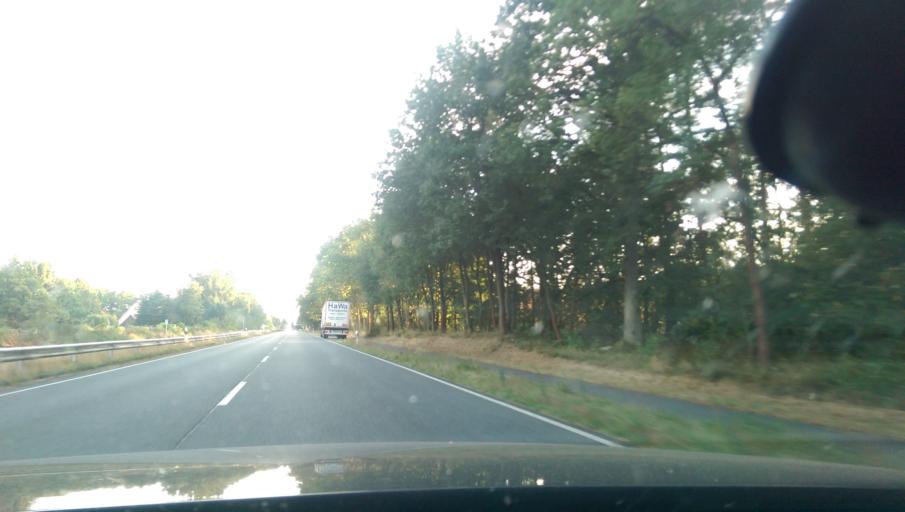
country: DE
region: Lower Saxony
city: Walsrode
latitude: 52.8306
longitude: 9.5938
